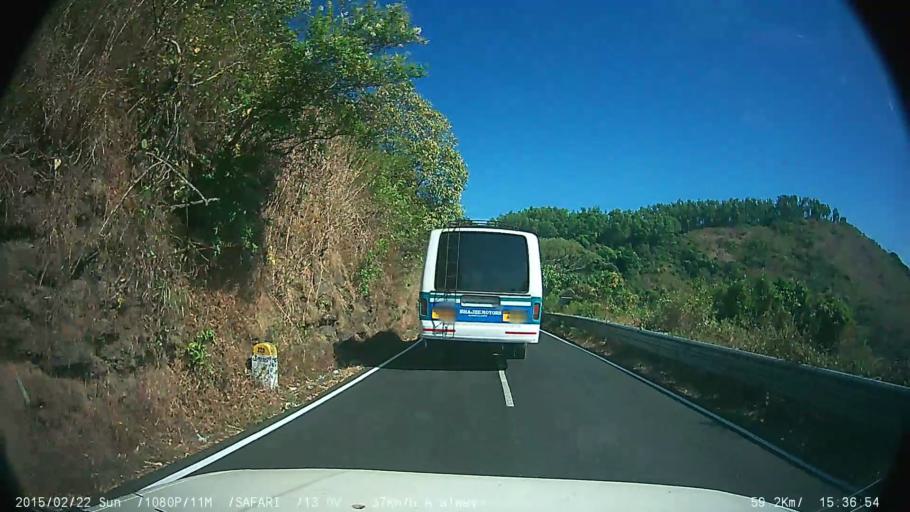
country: IN
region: Kerala
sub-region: Kottayam
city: Erattupetta
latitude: 9.5607
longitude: 76.9806
